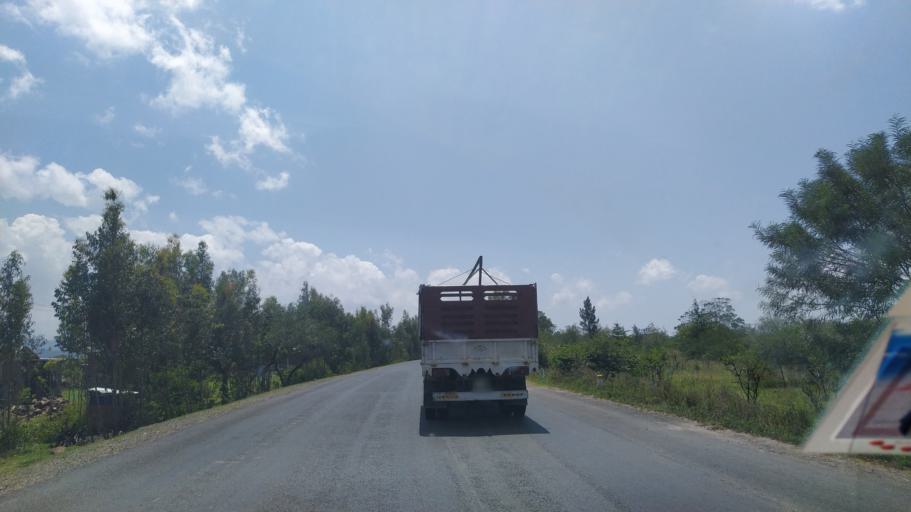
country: ET
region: Southern Nations, Nationalities, and People's Region
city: Butajira
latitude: 7.7807
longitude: 38.1387
